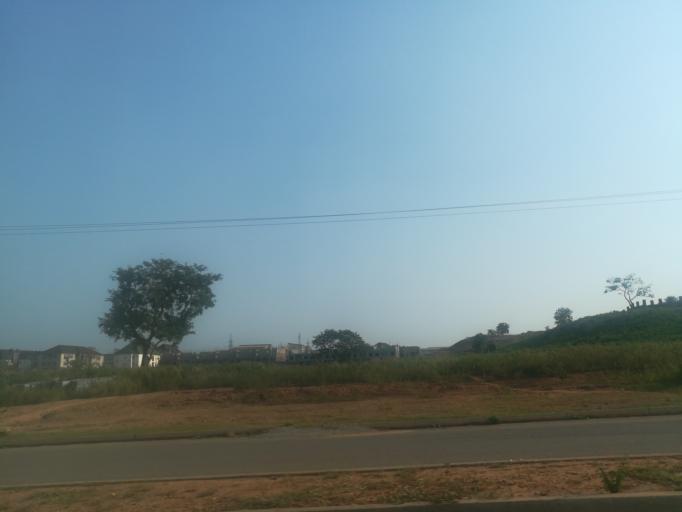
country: NG
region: Abuja Federal Capital Territory
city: Abuja
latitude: 9.0450
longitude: 7.4350
